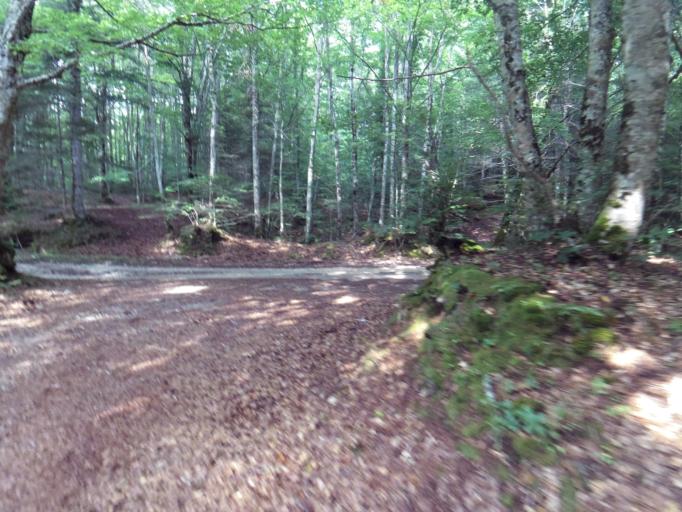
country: IT
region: Calabria
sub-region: Provincia di Vibo-Valentia
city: Nardodipace
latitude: 38.5229
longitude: 16.3811
